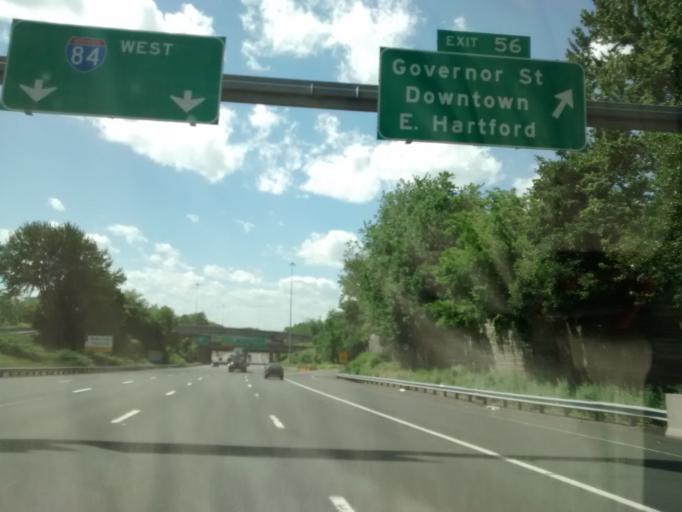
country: US
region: Connecticut
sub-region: Hartford County
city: Hartford
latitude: 41.7654
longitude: -72.6485
